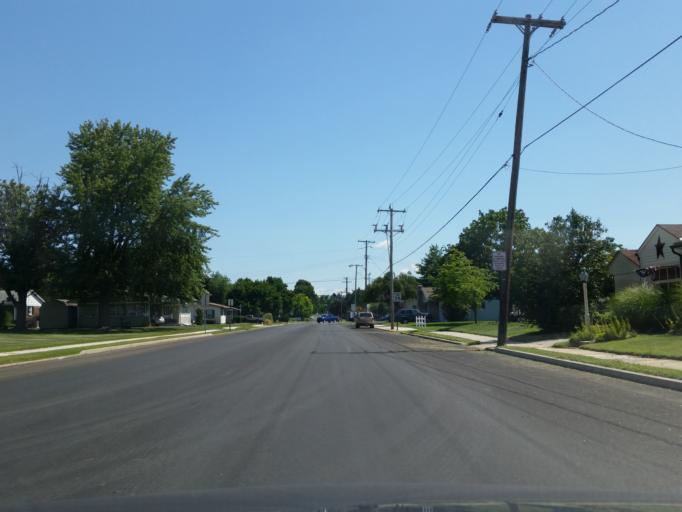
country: US
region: Pennsylvania
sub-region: Lebanon County
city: Palmyra
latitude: 40.3134
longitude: -76.5905
